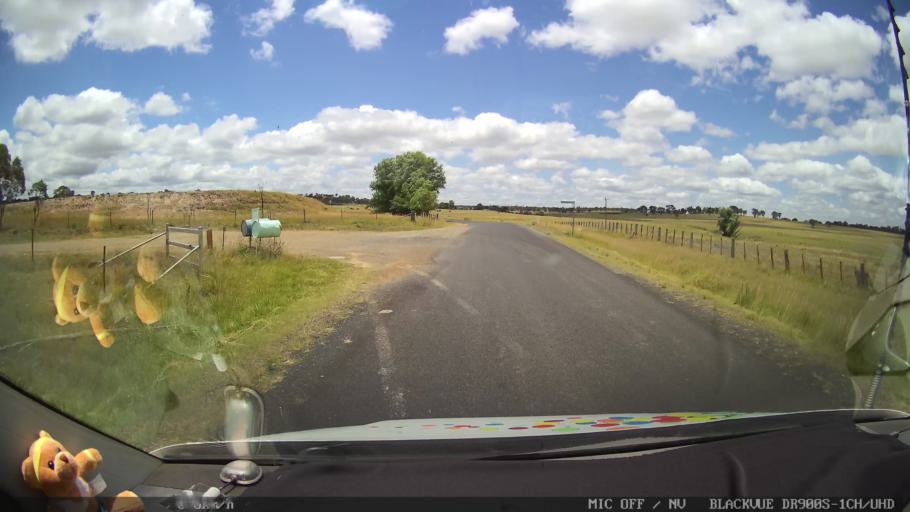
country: AU
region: New South Wales
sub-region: Glen Innes Severn
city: Glen Innes
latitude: -29.4224
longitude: 151.7376
